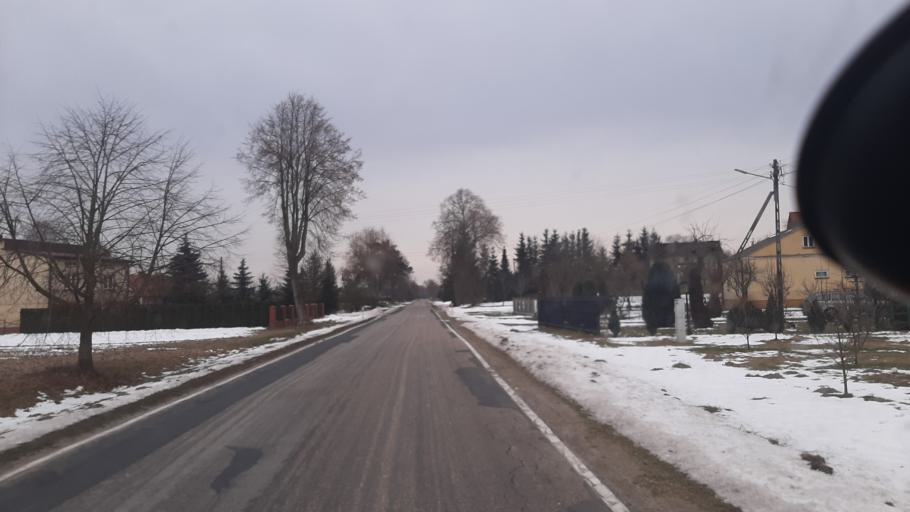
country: PL
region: Lublin Voivodeship
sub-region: Powiat lubartowski
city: Kamionka
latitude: 51.4582
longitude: 22.4207
